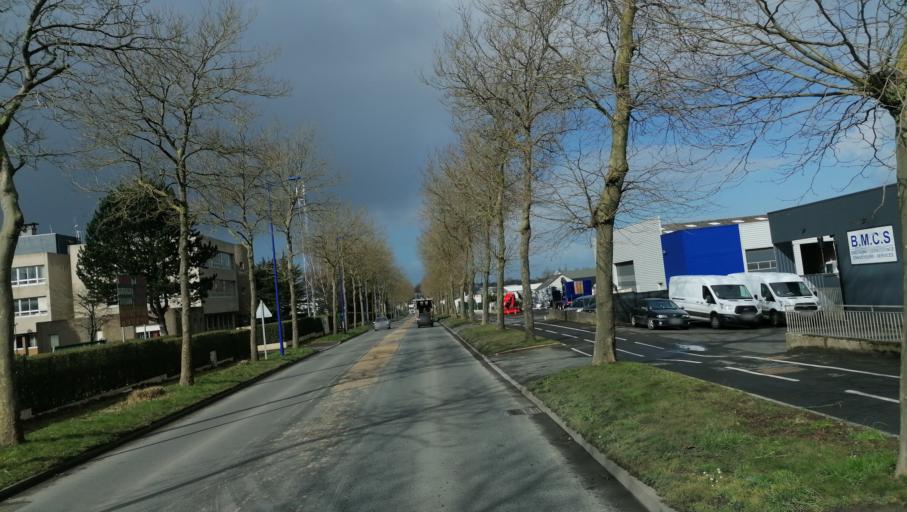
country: FR
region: Brittany
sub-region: Departement des Cotes-d'Armor
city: Ploufragan
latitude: 48.4651
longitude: -2.7869
